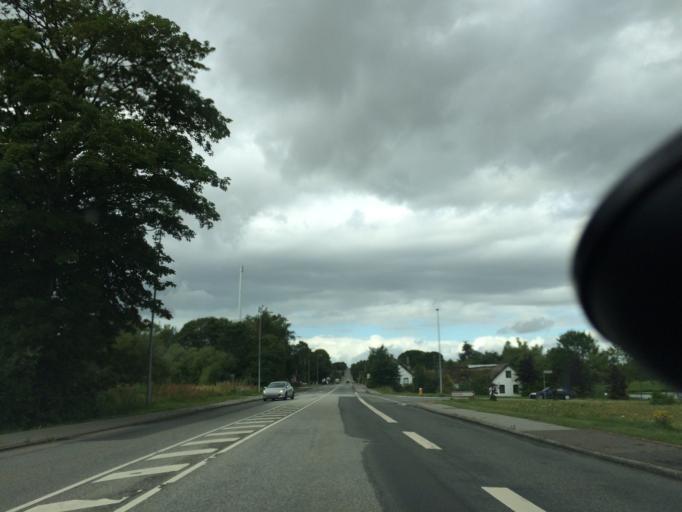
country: DK
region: Central Jutland
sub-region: Skanderborg Kommune
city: Galten
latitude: 56.1483
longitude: 9.9027
